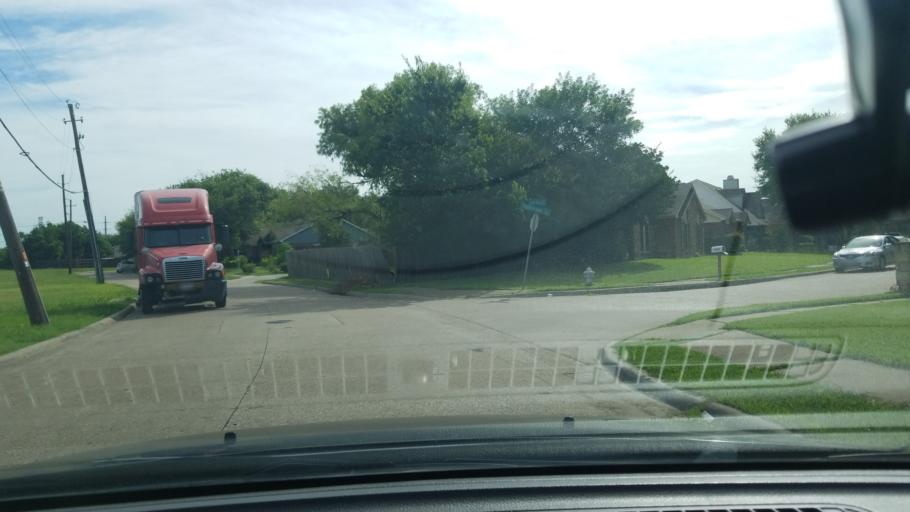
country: US
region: Texas
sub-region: Dallas County
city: Balch Springs
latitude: 32.7731
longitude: -96.6636
